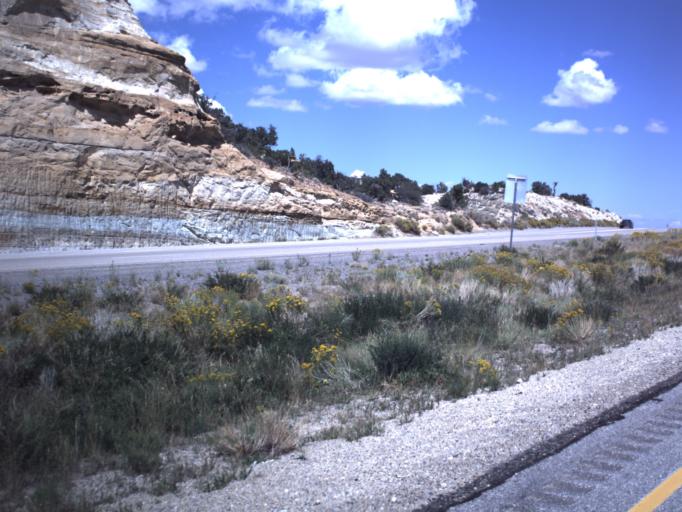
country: US
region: Utah
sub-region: Emery County
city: Ferron
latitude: 38.8602
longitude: -110.8171
